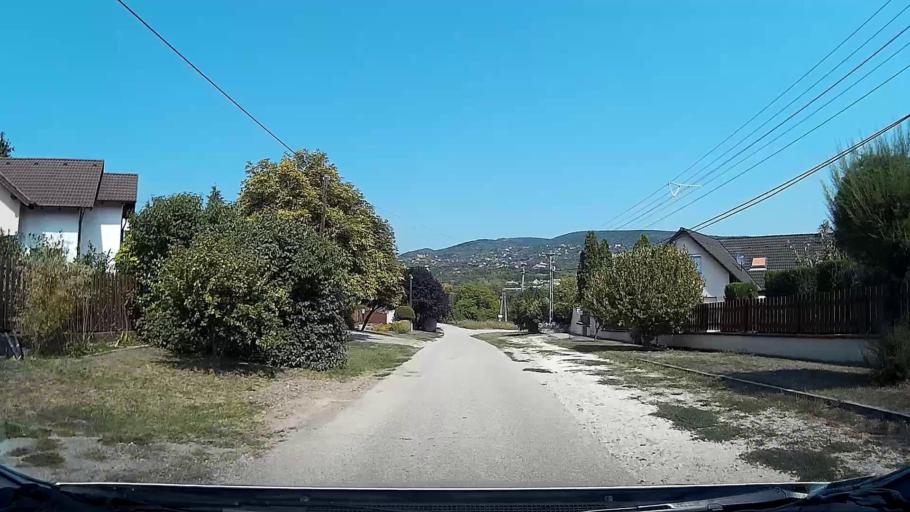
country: HU
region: Pest
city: Szentendre
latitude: 47.6847
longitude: 19.0526
